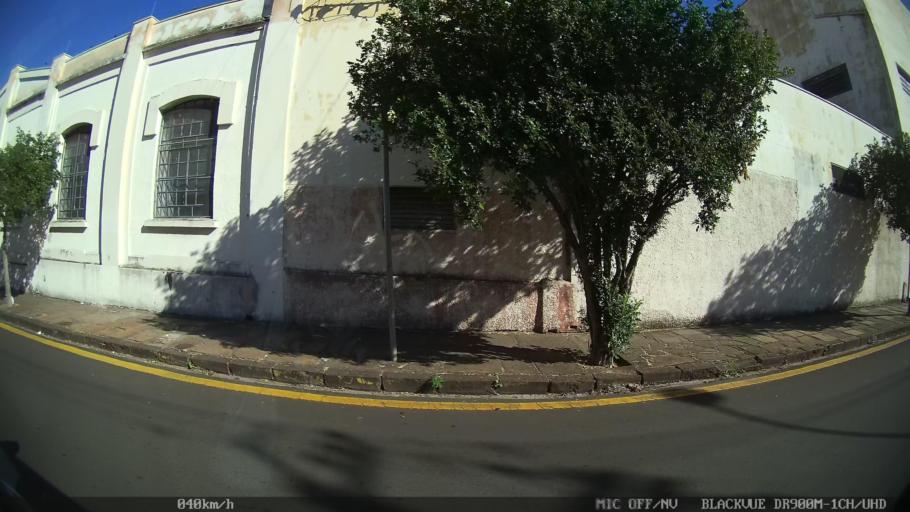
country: BR
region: Sao Paulo
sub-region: Franca
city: Franca
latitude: -20.5355
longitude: -47.3984
